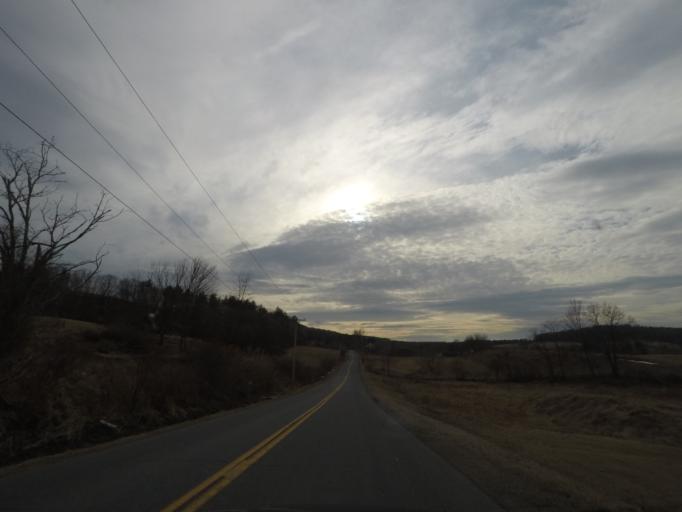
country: US
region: New York
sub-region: Rensselaer County
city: Hoosick Falls
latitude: 42.9100
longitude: -73.3702
